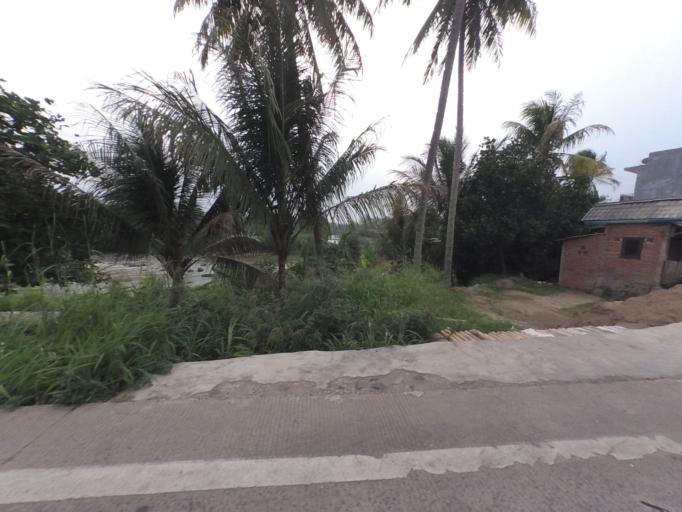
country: ID
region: West Java
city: Sidoger Lebak
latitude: -6.5641
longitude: 106.5841
